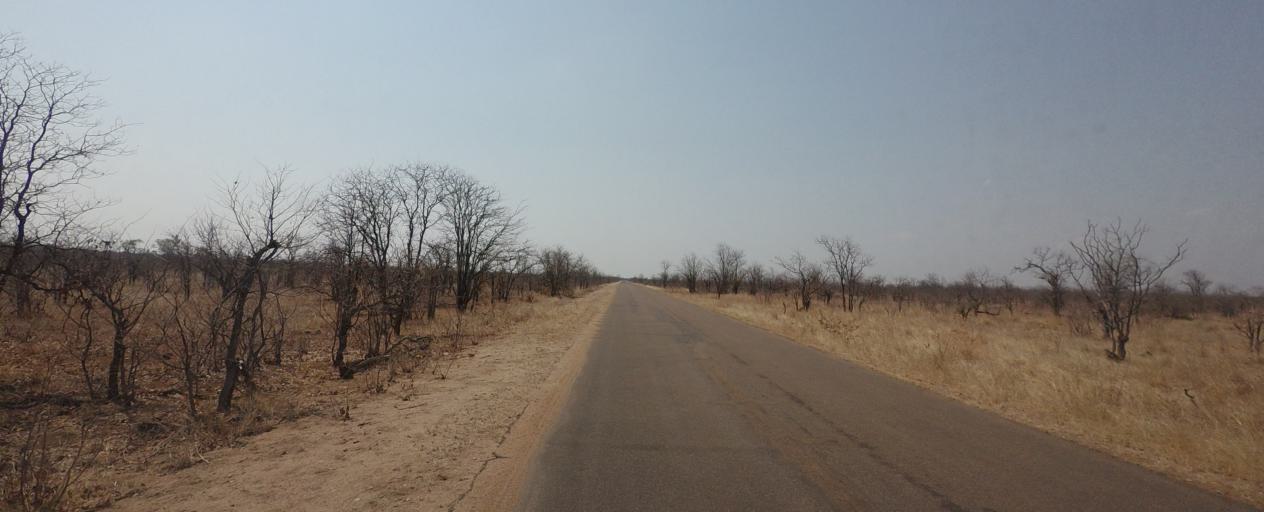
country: ZA
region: Limpopo
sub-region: Mopani District Municipality
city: Giyani
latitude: -23.3636
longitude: 31.3196
